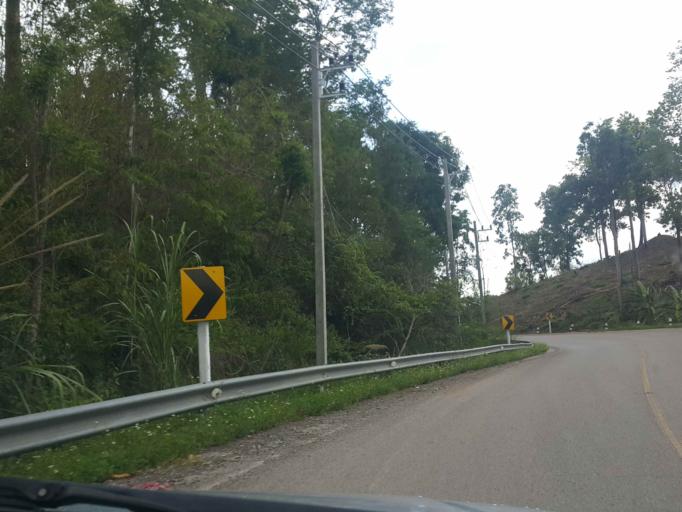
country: TH
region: Lampang
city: Ngao
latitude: 18.9336
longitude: 100.0893
